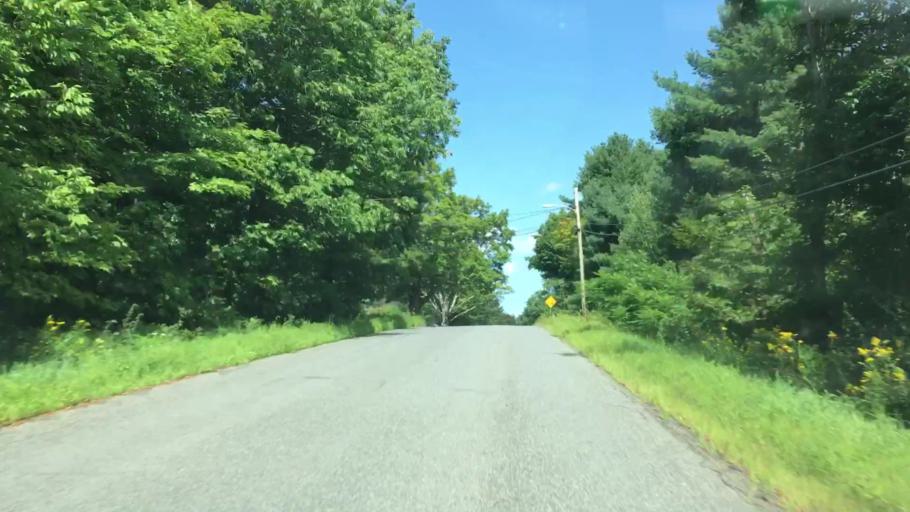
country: US
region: Maine
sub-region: Kennebec County
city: Manchester
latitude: 44.3658
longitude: -69.8160
